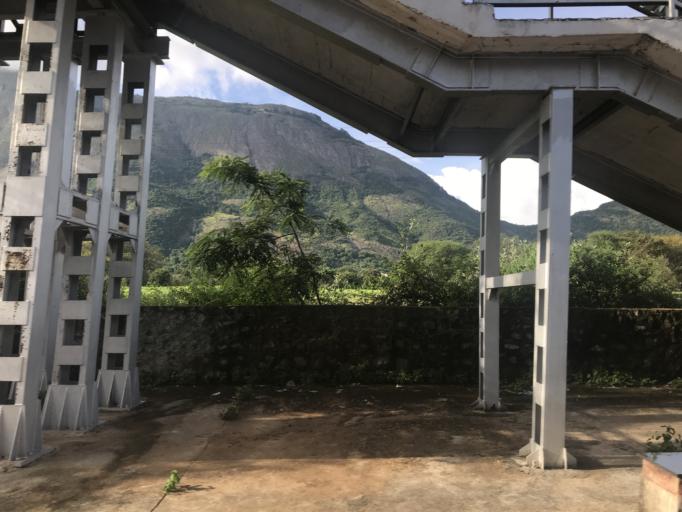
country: IN
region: Tamil Nadu
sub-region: Coimbatore
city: Madukkarai
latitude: 10.8984
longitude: 76.8955
